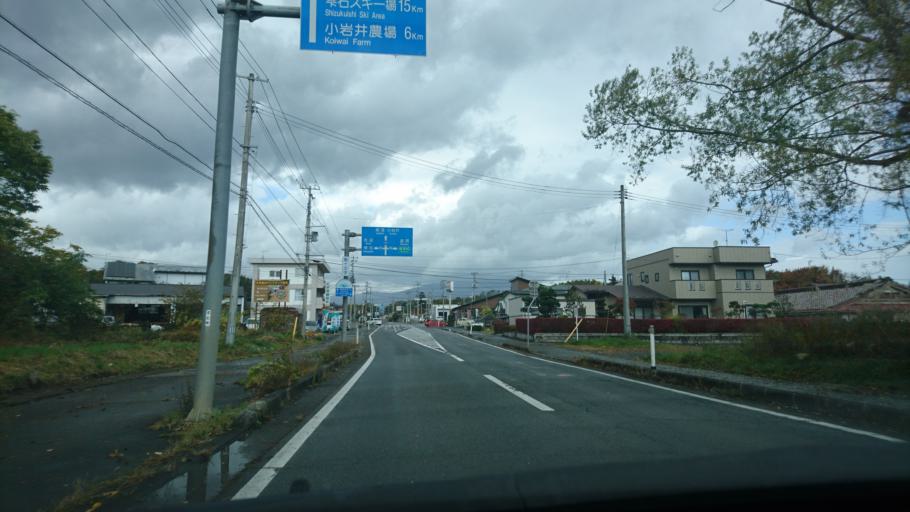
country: JP
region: Iwate
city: Shizukuishi
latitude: 39.6966
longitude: 141.0231
